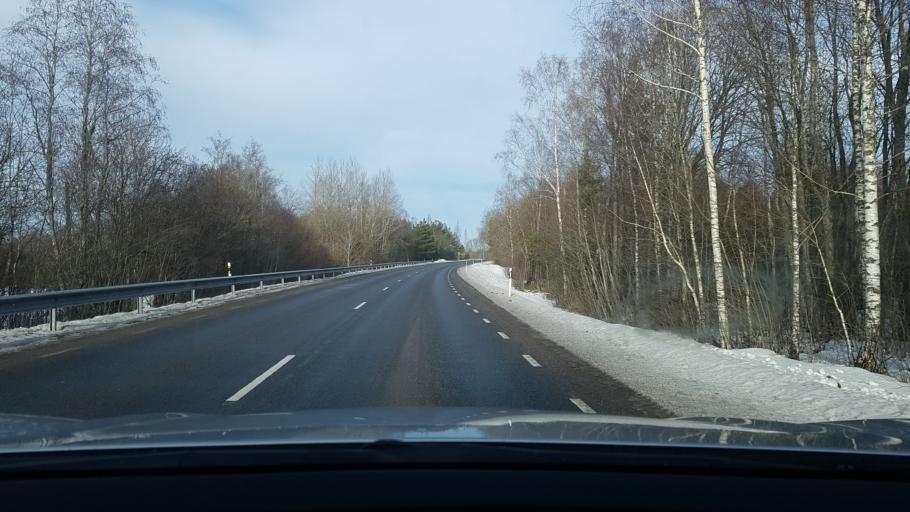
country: EE
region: Saare
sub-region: Kuressaare linn
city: Kuressaare
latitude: 58.3039
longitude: 22.5393
